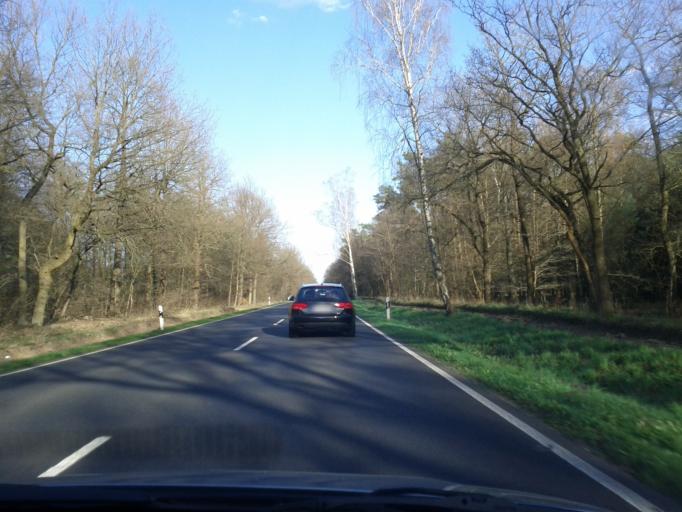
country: DE
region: Brandenburg
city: Rauen
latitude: 52.3703
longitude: 14.0156
